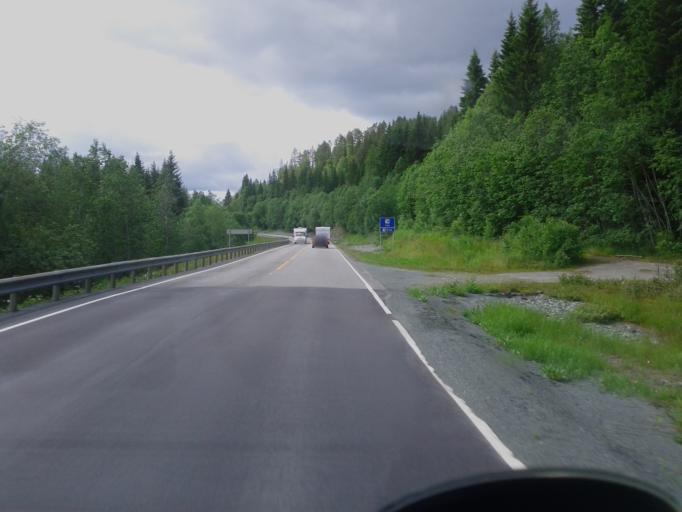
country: NO
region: Nord-Trondelag
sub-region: Grong
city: Grong
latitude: 64.5407
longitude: 12.4485
